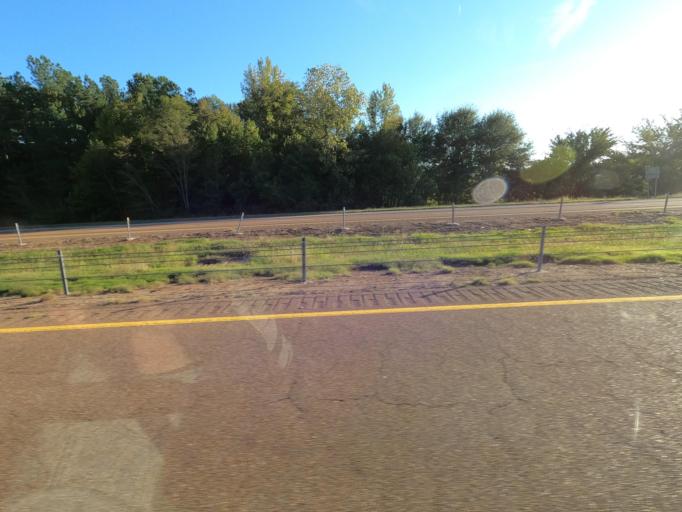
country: US
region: Tennessee
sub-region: Shelby County
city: Millington
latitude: 35.3081
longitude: -89.8052
